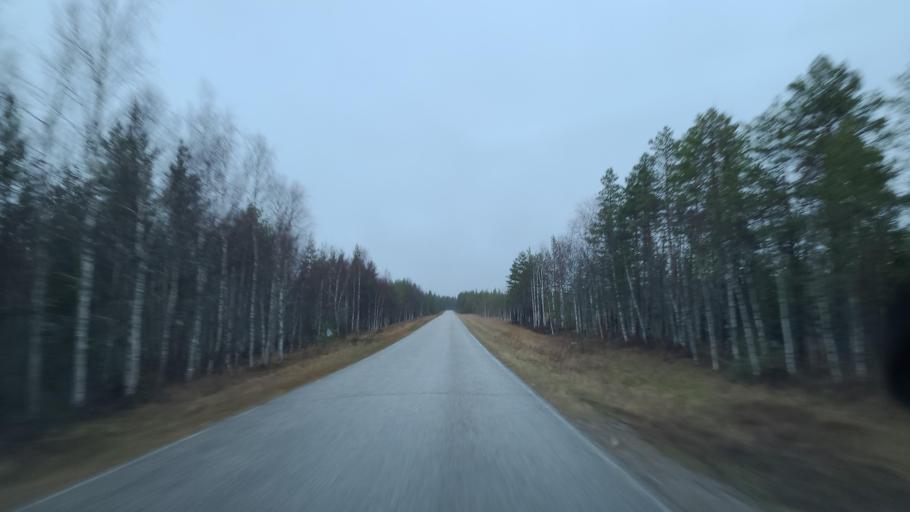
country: FI
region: Lapland
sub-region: Kemi-Tornio
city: Simo
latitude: 65.9122
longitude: 25.2017
